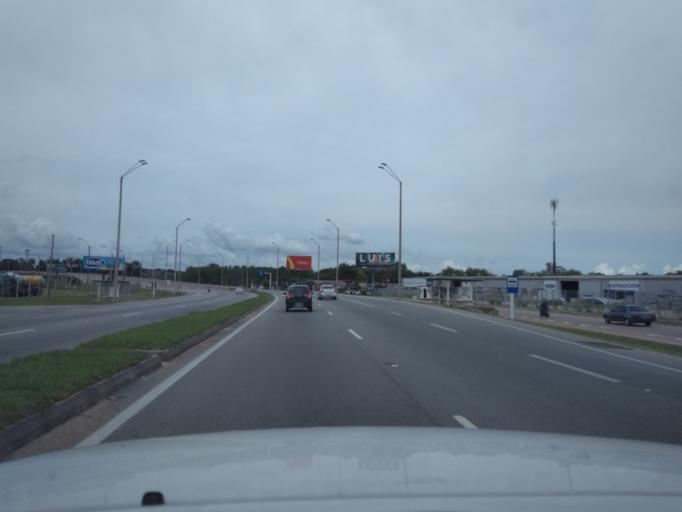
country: UY
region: Canelones
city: Barra de Carrasco
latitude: -34.8437
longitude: -56.0171
